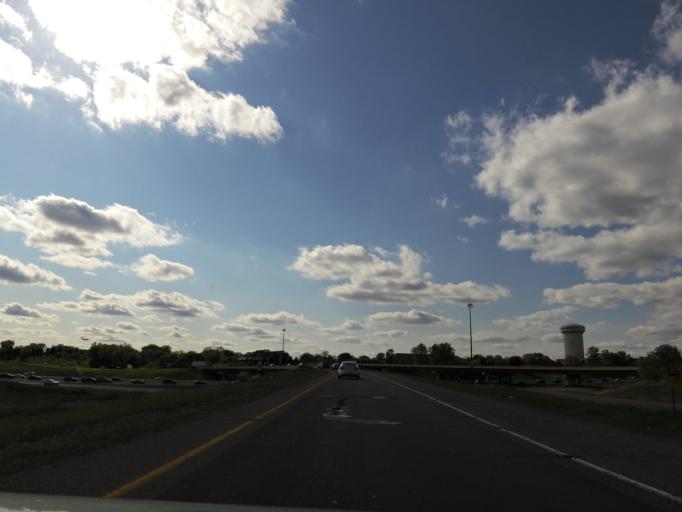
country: US
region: Minnesota
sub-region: Dakota County
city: Mendota Heights
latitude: 44.8640
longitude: -93.1423
